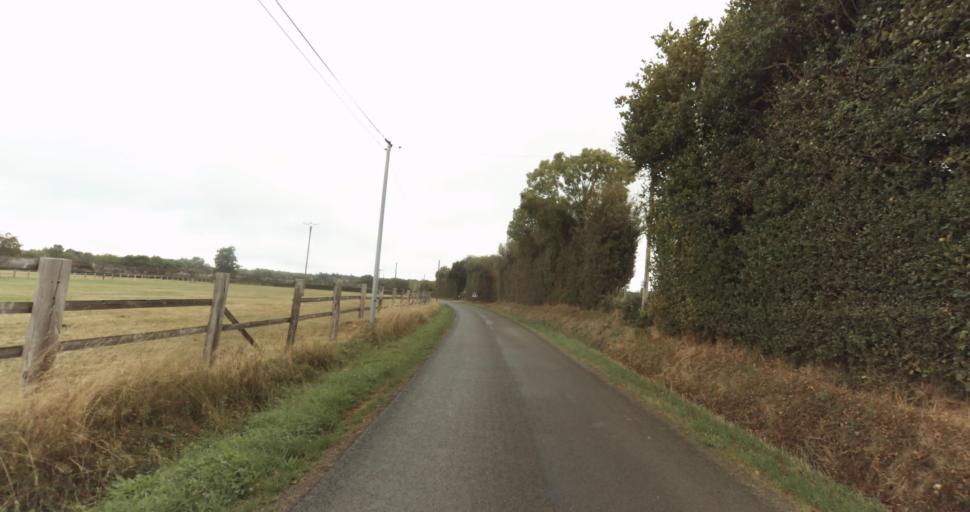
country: FR
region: Lower Normandy
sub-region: Departement de l'Orne
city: Sainte-Gauburge-Sainte-Colombe
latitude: 48.7427
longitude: 0.4717
